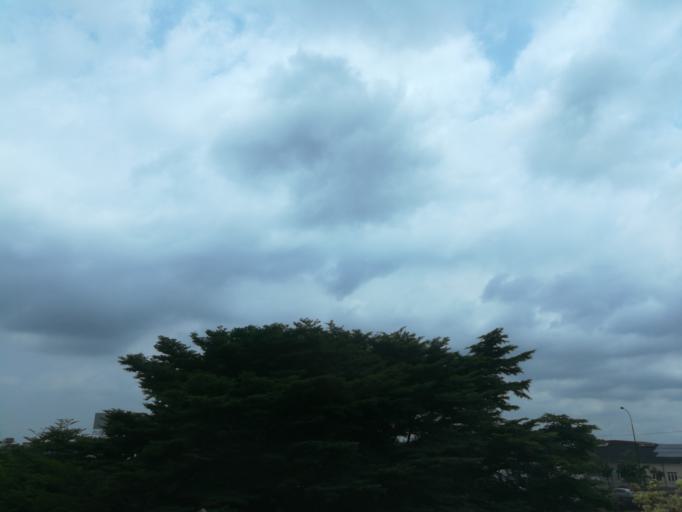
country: NG
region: Lagos
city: Ikeja
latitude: 6.5897
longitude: 3.3369
